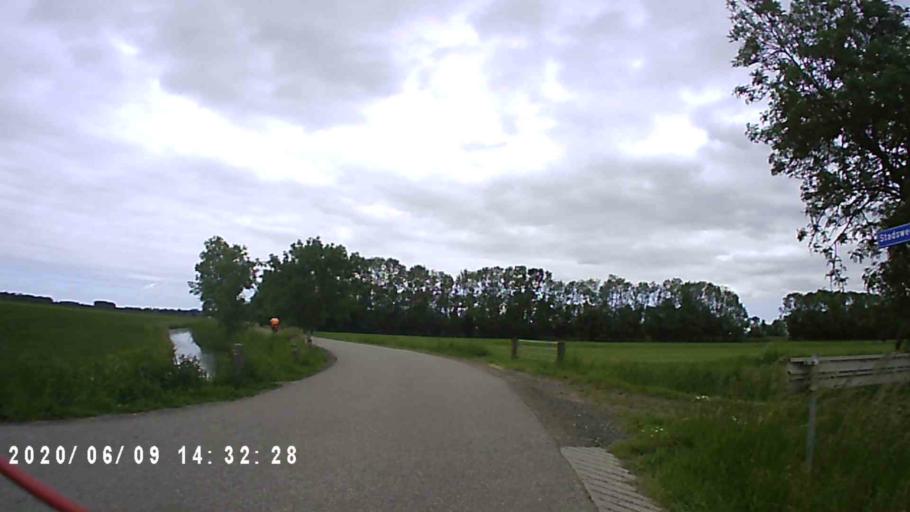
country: NL
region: Groningen
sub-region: Gemeente Bedum
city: Bedum
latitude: 53.3194
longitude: 6.5917
